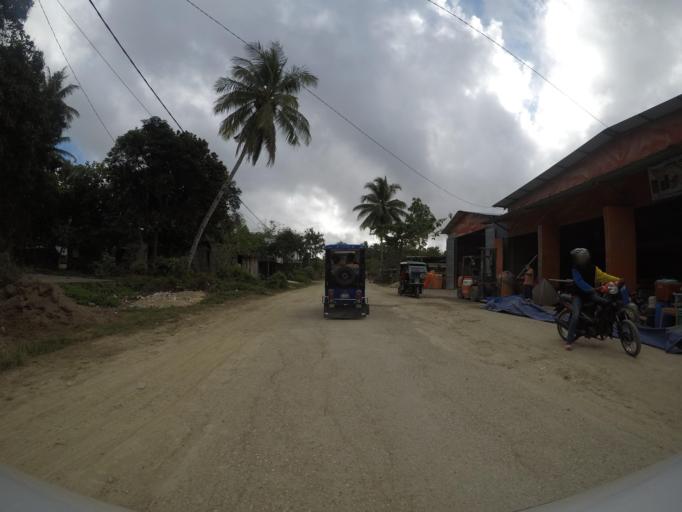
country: TL
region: Lautem
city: Lospalos
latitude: -8.5157
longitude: 127.0011
